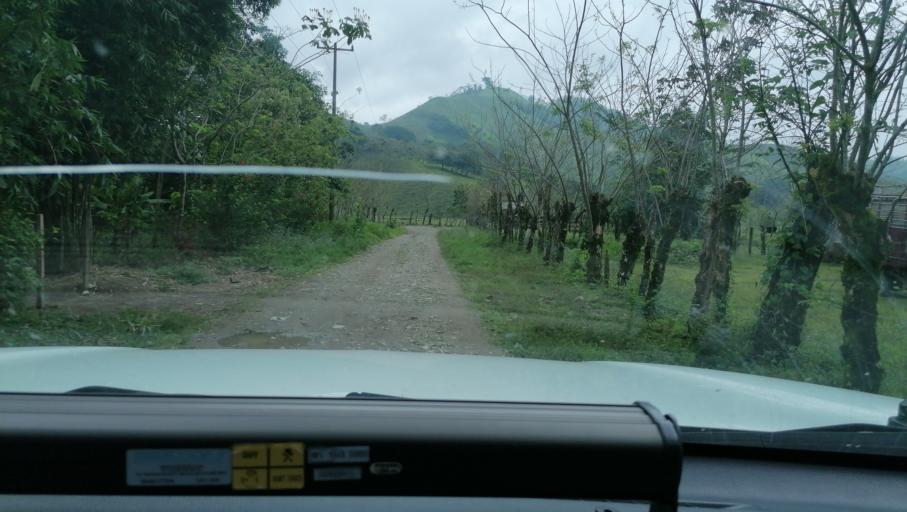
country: MX
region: Chiapas
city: Ixtacomitan
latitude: 17.3673
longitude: -93.1830
